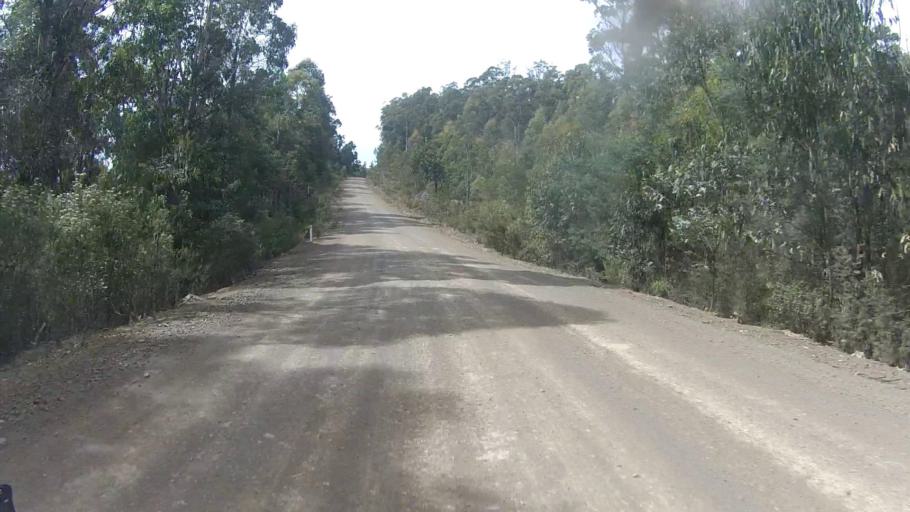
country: AU
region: Tasmania
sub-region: Sorell
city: Sorell
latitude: -42.7530
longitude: 147.8278
